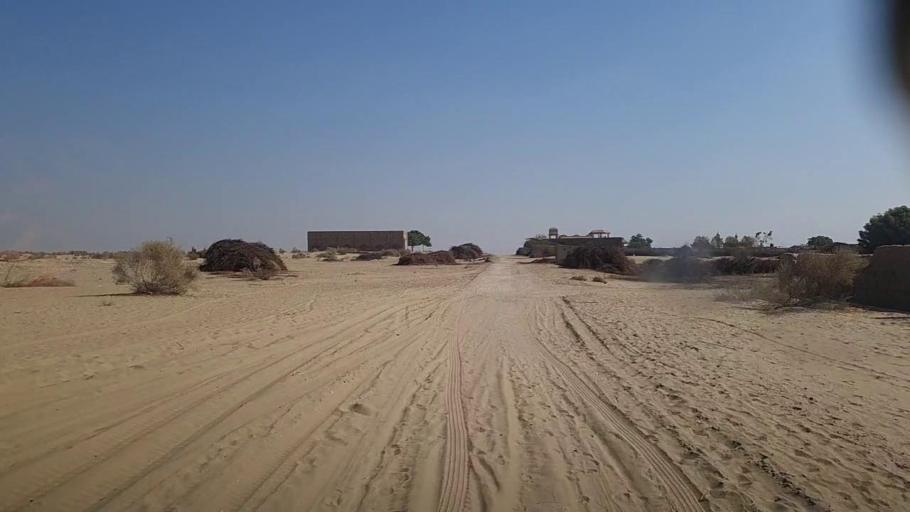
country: PK
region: Sindh
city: Khairpur
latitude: 28.0030
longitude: 69.8555
